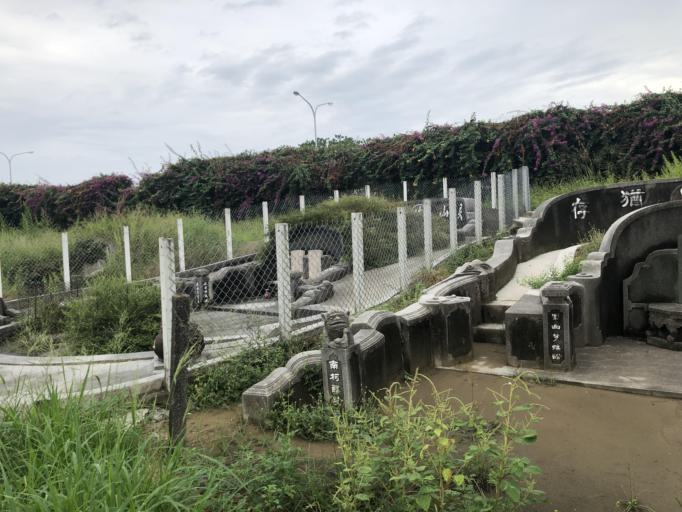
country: TW
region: Taiwan
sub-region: Tainan
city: Tainan
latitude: 22.9658
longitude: 120.1981
